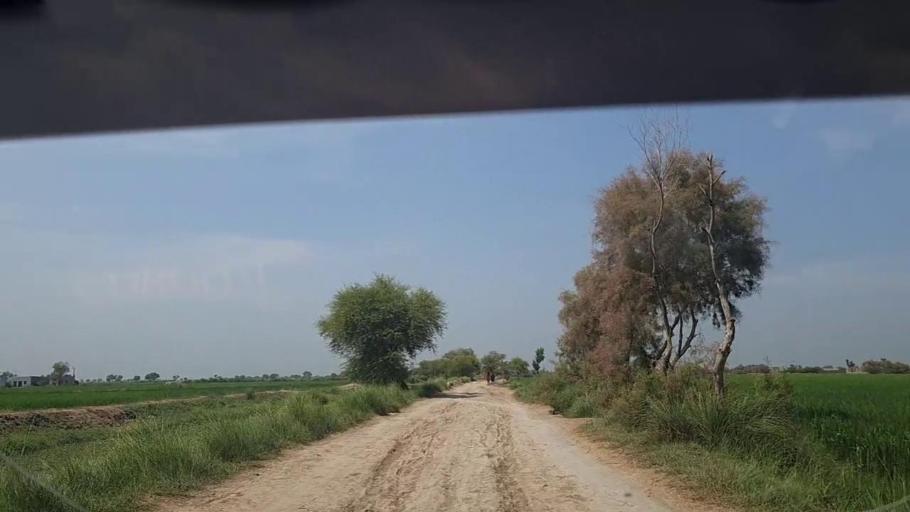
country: PK
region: Sindh
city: Thul
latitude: 28.1857
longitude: 68.7201
